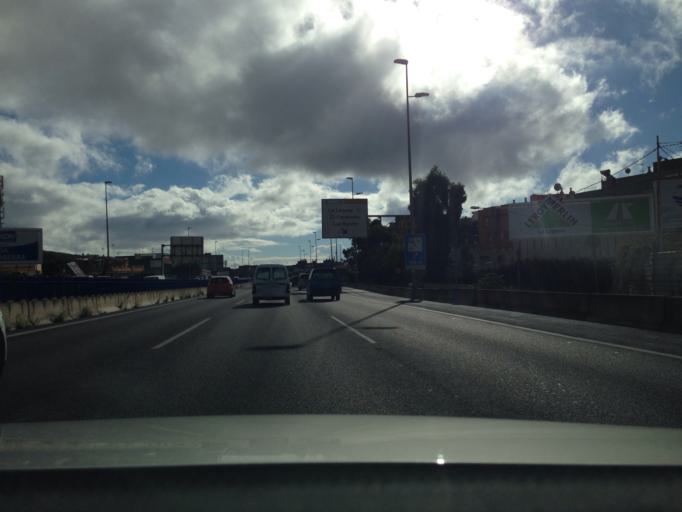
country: ES
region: Canary Islands
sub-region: Provincia de Santa Cruz de Tenerife
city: La Laguna
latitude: 28.4879
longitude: -16.3280
